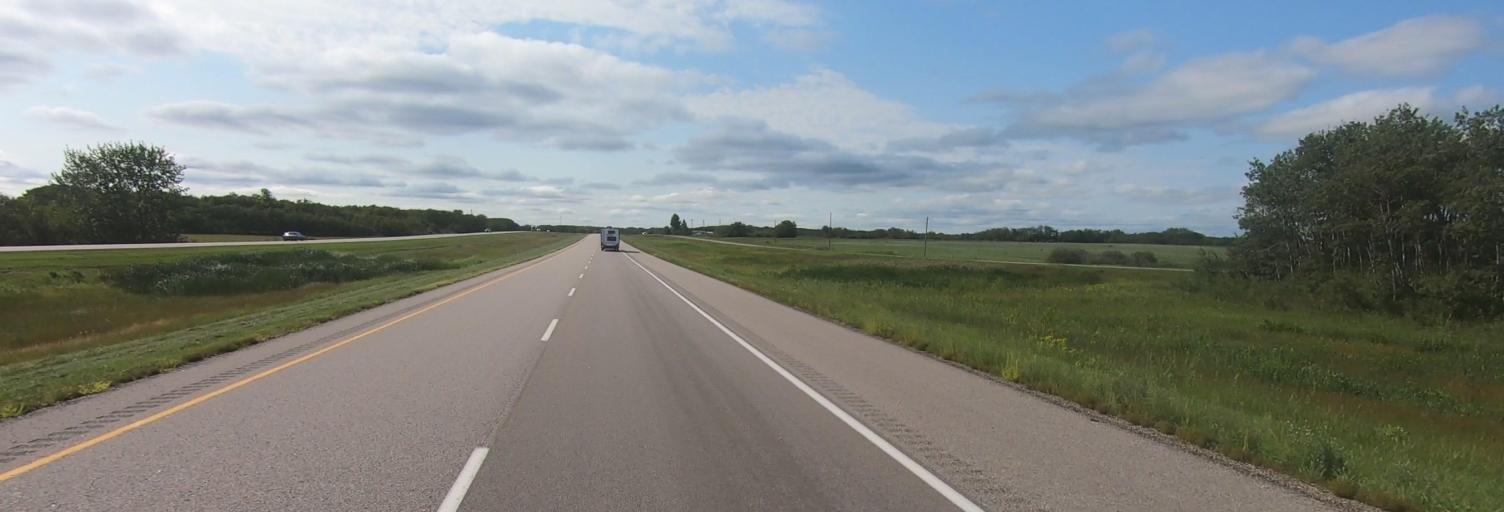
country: CA
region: Manitoba
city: Virden
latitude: 49.7980
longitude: -100.8194
